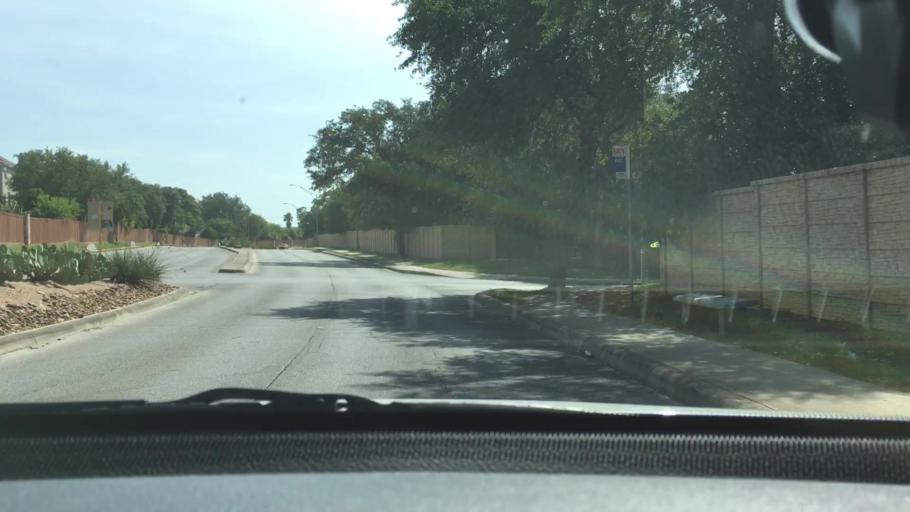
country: US
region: Texas
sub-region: Bexar County
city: Live Oak
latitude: 29.5882
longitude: -98.4002
